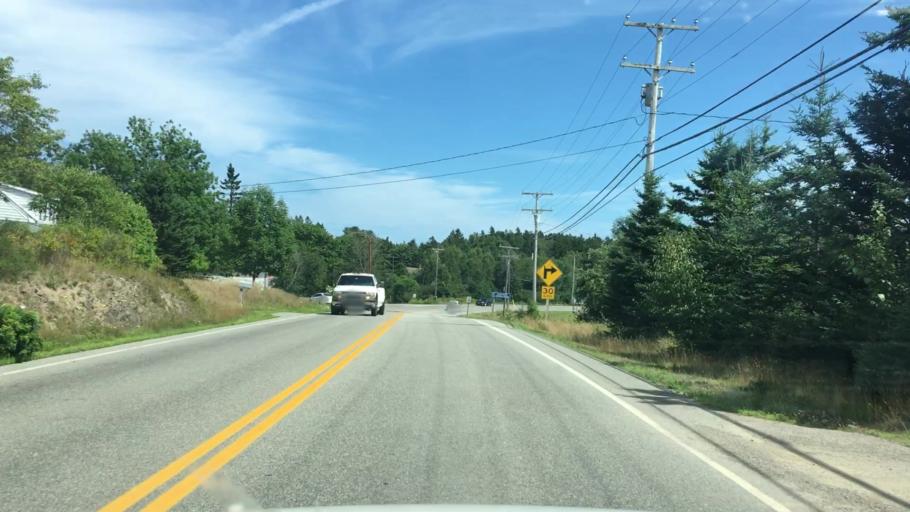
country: US
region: Maine
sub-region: Washington County
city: Eastport
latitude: 44.9128
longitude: -67.0026
